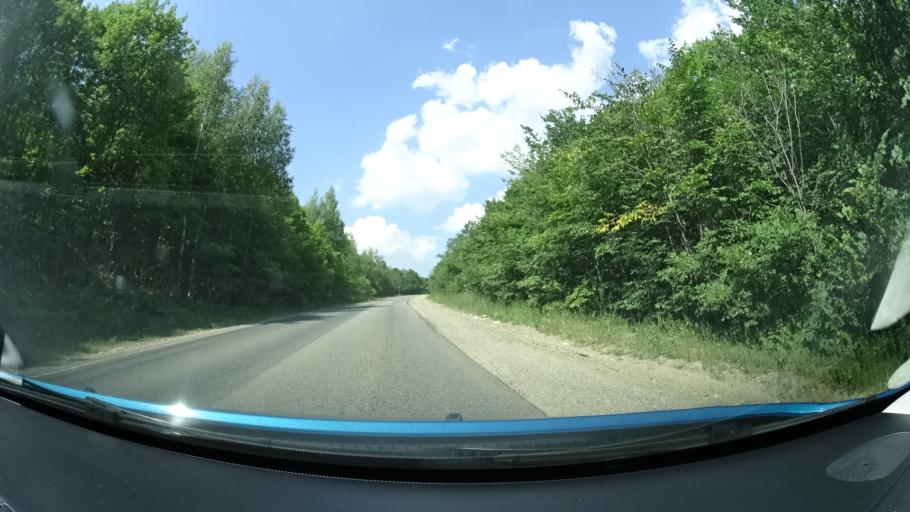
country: RU
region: Bashkortostan
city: Oktyabr'skiy
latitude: 54.4598
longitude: 53.5782
